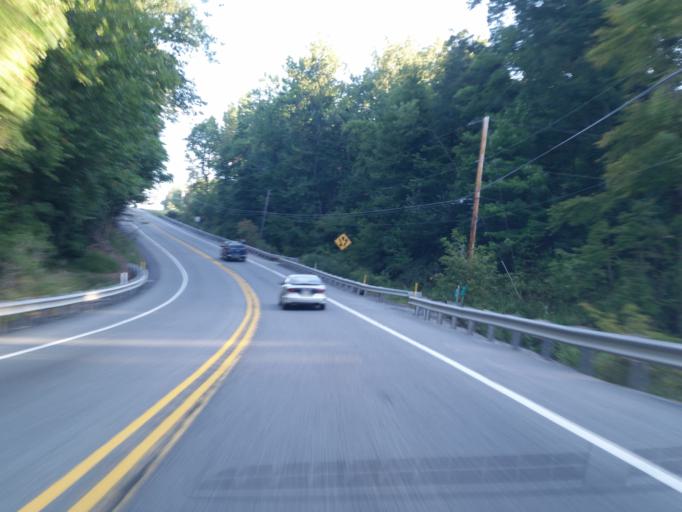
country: US
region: Pennsylvania
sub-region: Lancaster County
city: Willow Street
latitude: 39.9132
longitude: -76.2436
